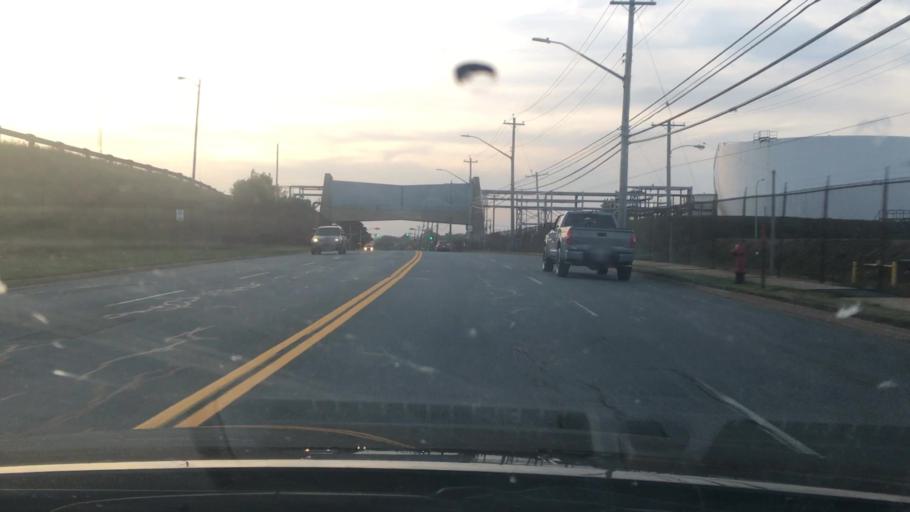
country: CA
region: Nova Scotia
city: Halifax
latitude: 44.6400
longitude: -63.5322
